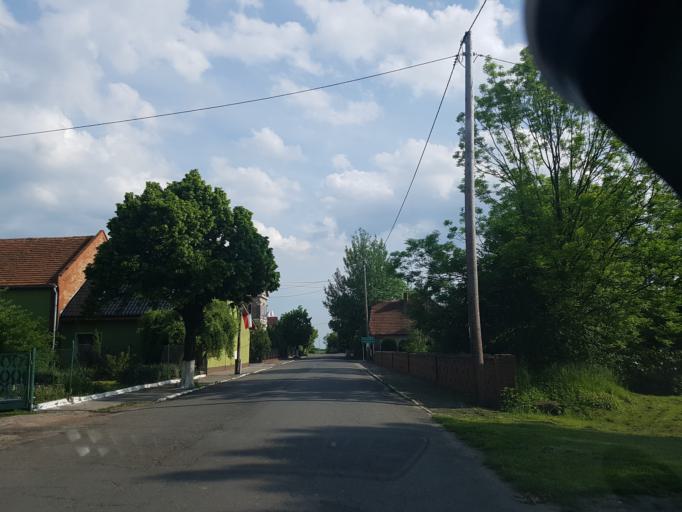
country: PL
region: Lower Silesian Voivodeship
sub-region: Powiat strzelinski
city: Wiazow
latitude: 50.8674
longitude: 17.1564
